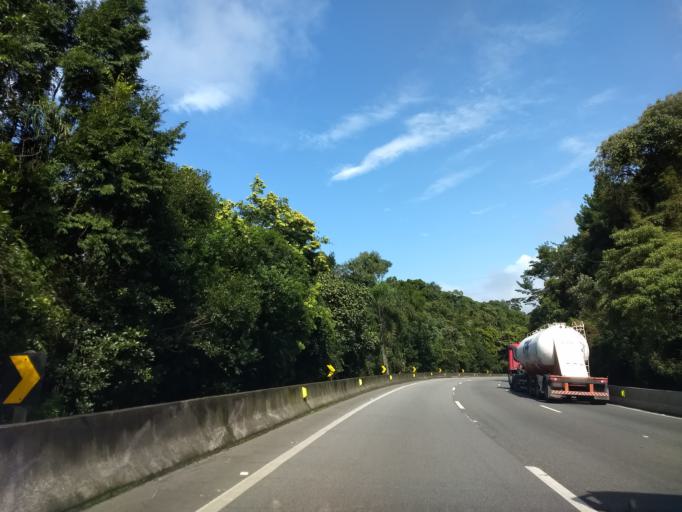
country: BR
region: Parana
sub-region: Sao Jose Dos Pinhais
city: Sao Jose dos Pinhais
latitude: -25.8424
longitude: -49.0333
